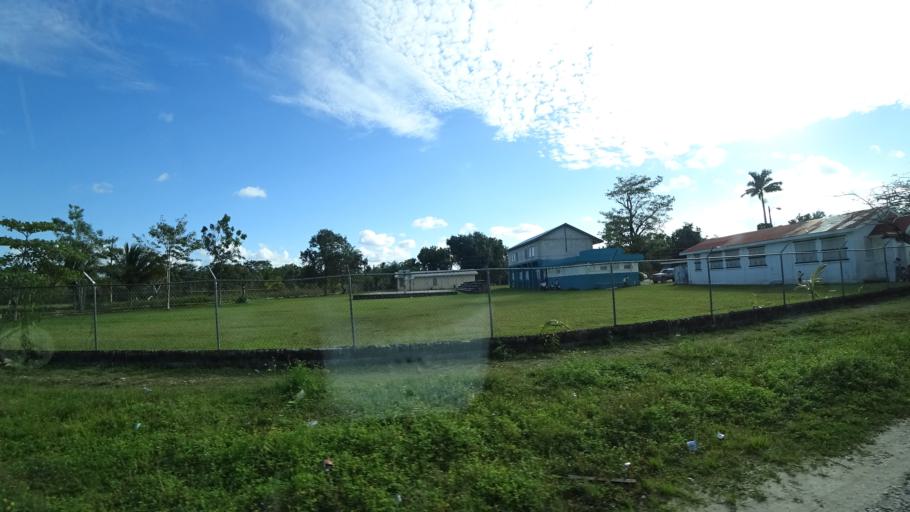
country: BZ
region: Belize
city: Belize City
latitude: 17.5692
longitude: -88.4030
